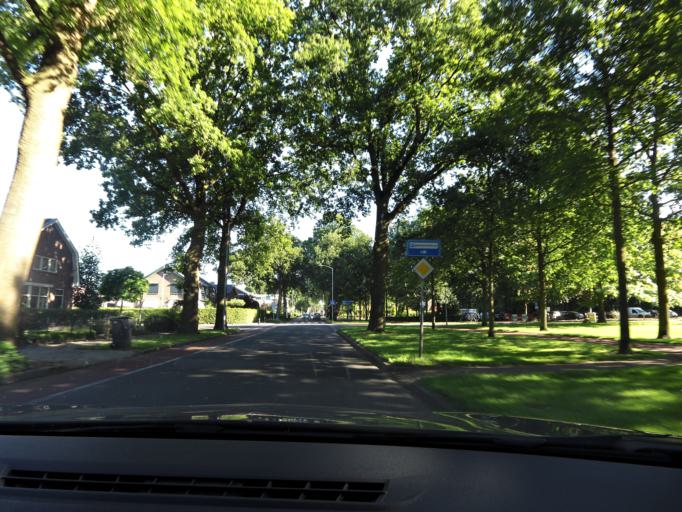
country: NL
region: Gelderland
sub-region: Gemeente Voorst
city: Twello
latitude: 52.2362
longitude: 6.1085
